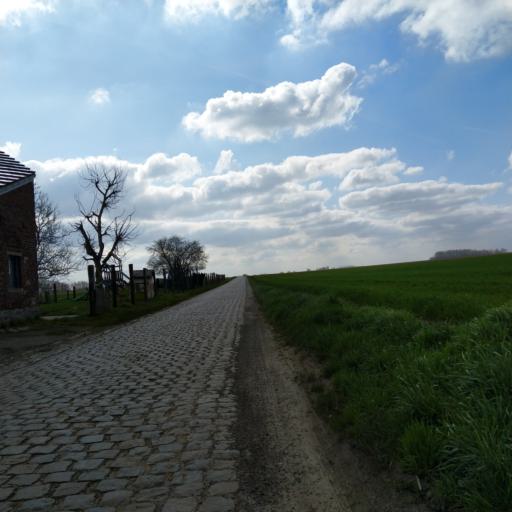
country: BE
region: Wallonia
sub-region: Province du Hainaut
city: Jurbise
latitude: 50.5543
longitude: 3.9503
